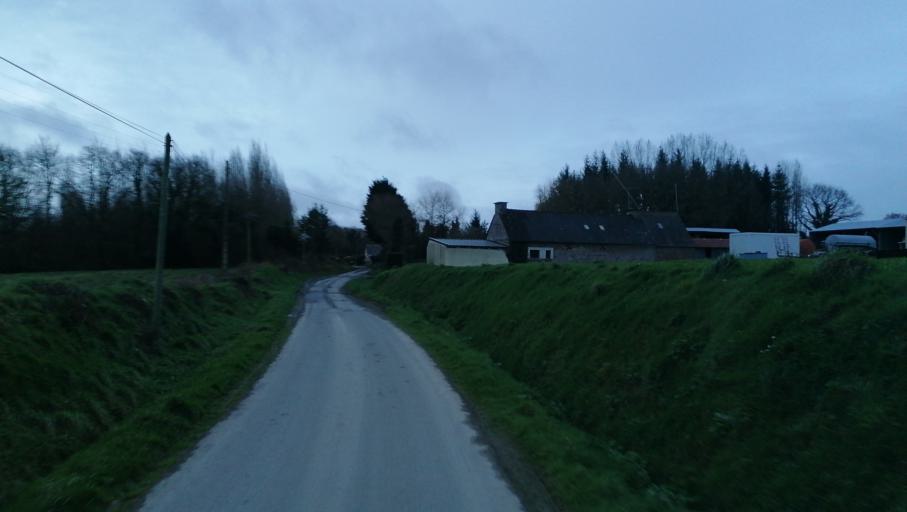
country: FR
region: Brittany
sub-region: Departement des Cotes-d'Armor
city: Goudelin
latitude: 48.5761
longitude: -3.0532
